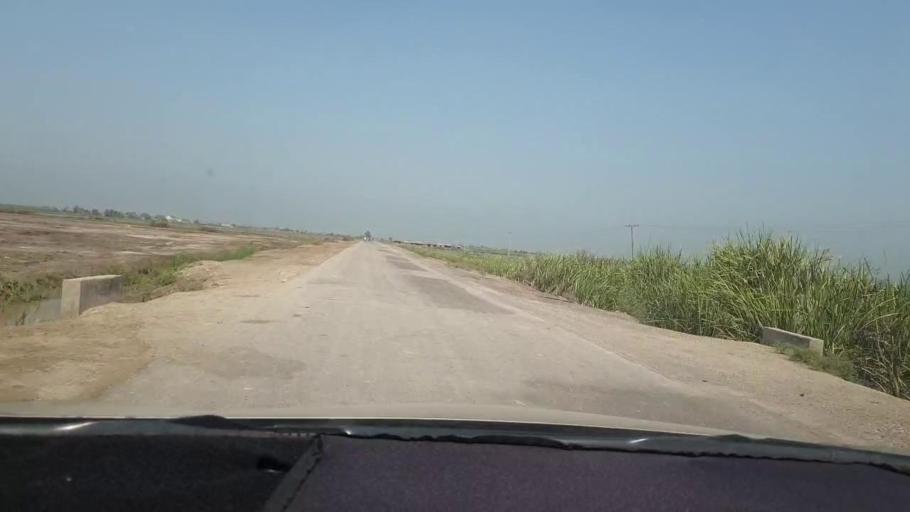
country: PK
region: Sindh
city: Miro Khan
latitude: 27.8317
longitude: 68.0143
